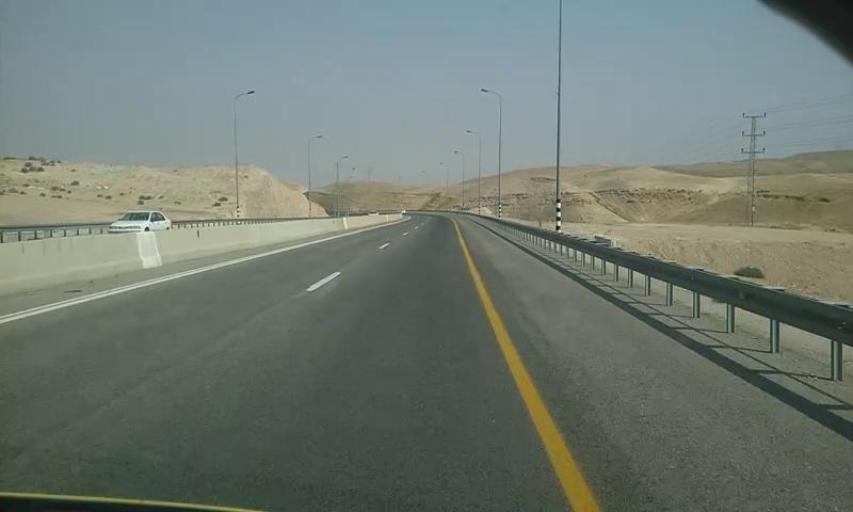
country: PS
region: West Bank
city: Jericho
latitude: 31.7988
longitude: 35.4328
